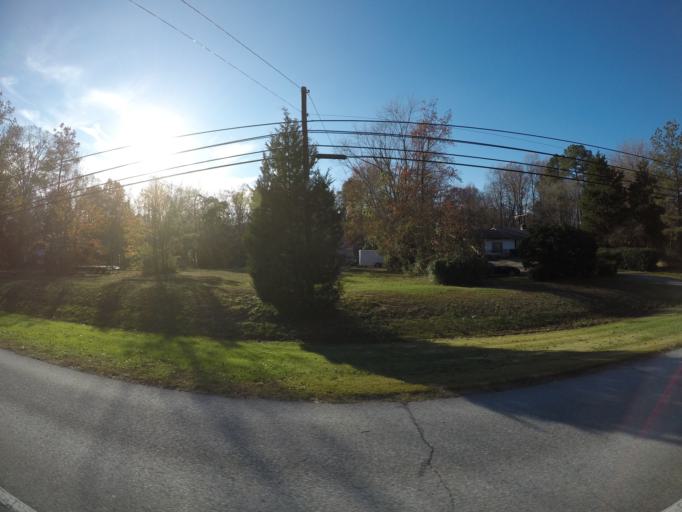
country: US
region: Maryland
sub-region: Saint Mary's County
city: Leonardtown
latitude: 38.3264
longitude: -76.6765
